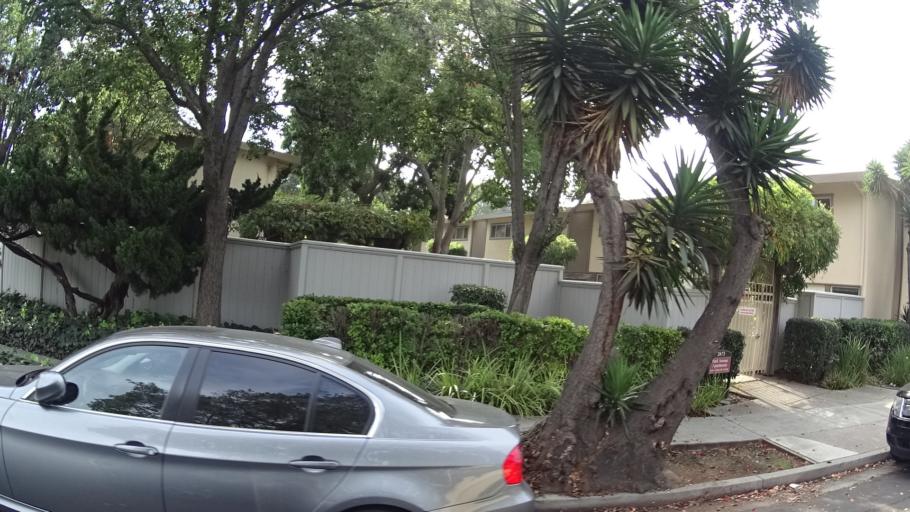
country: US
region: California
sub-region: Santa Clara County
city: Santa Clara
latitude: 37.3440
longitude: -121.9366
